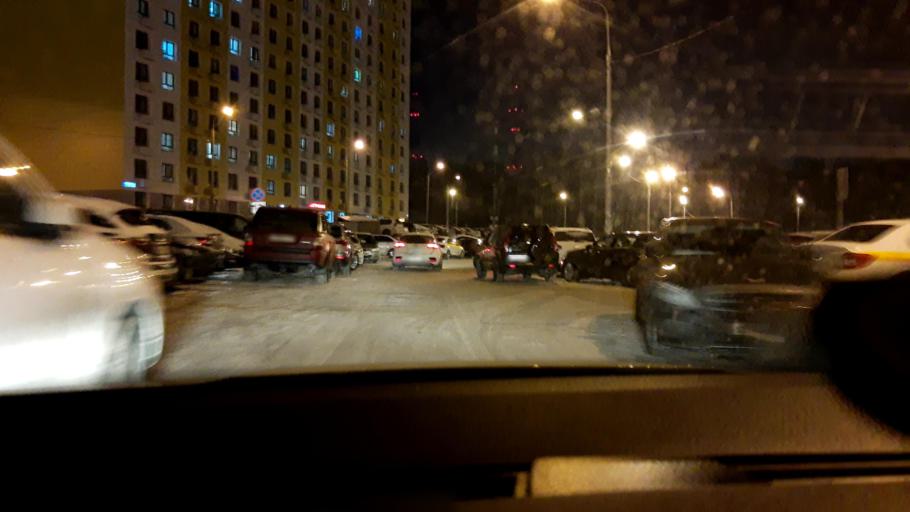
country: RU
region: Moscow
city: Khimki
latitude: 55.8759
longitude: 37.3929
